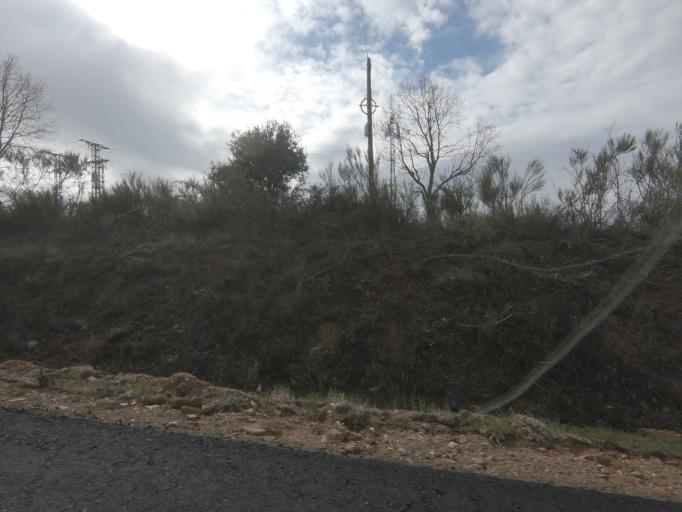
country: ES
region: Castille and Leon
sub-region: Provincia de Salamanca
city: Robleda
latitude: 40.3621
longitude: -6.6231
